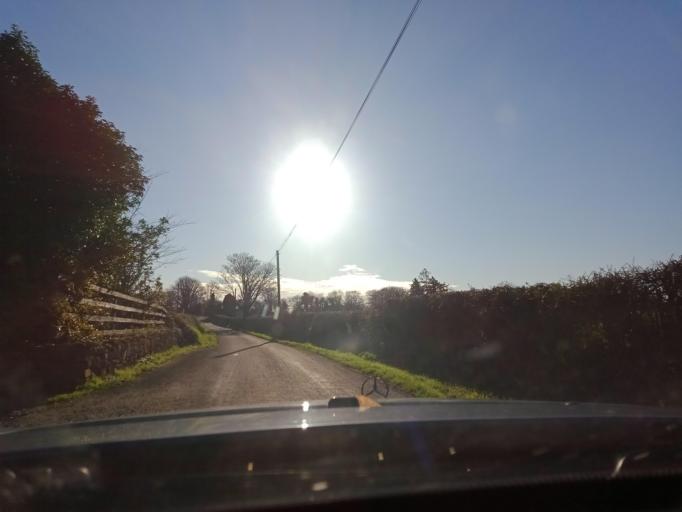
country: IE
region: Leinster
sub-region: Kilkenny
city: Mooncoin
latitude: 52.3022
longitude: -7.2230
